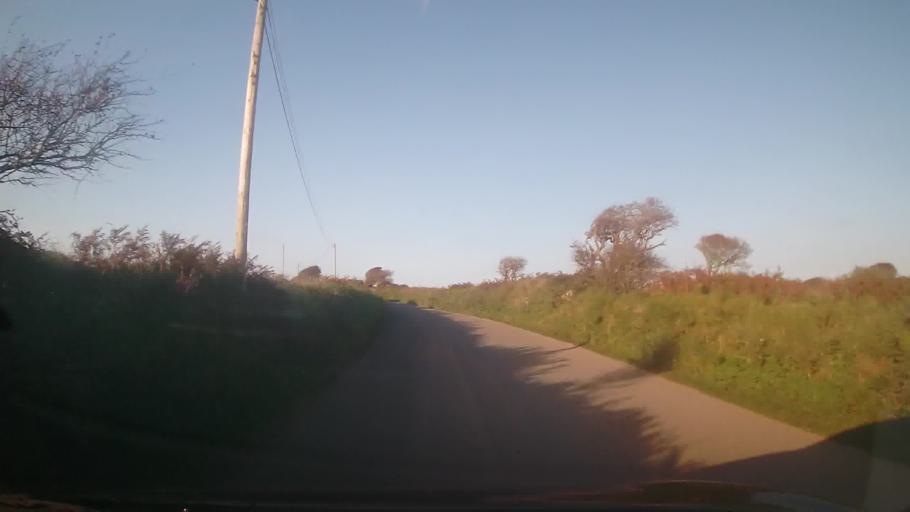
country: GB
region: Wales
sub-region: Pembrokeshire
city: Saint David's
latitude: 51.9057
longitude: -5.2433
